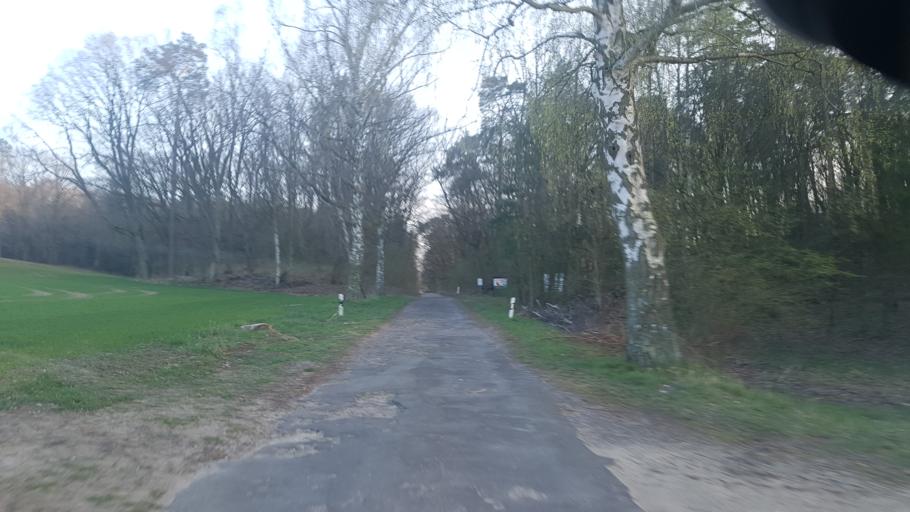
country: DE
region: Brandenburg
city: Gramzow
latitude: 53.2104
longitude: 13.9374
